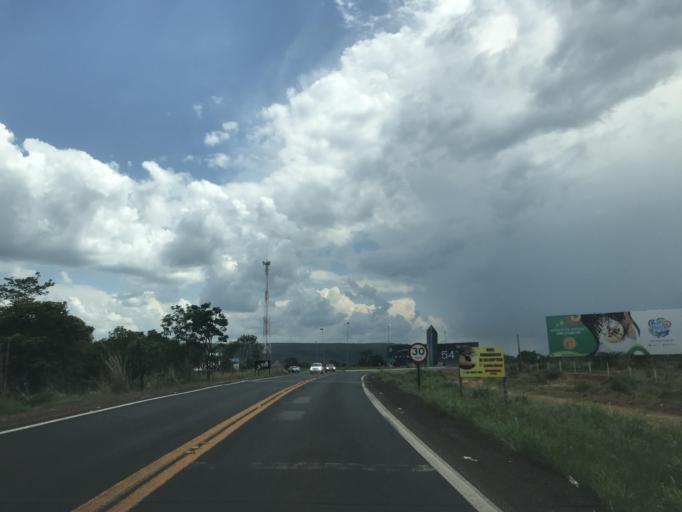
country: BR
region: Goias
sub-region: Caldas Novas
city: Caldas Novas
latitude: -17.6985
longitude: -48.7075
